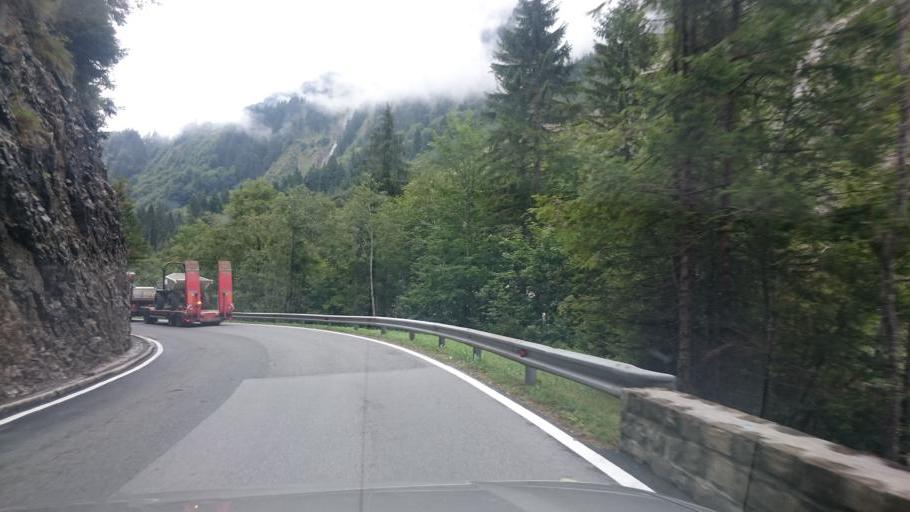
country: AT
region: Vorarlberg
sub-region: Politischer Bezirk Bregenz
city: Schoppernau
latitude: 47.2868
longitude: 10.0464
